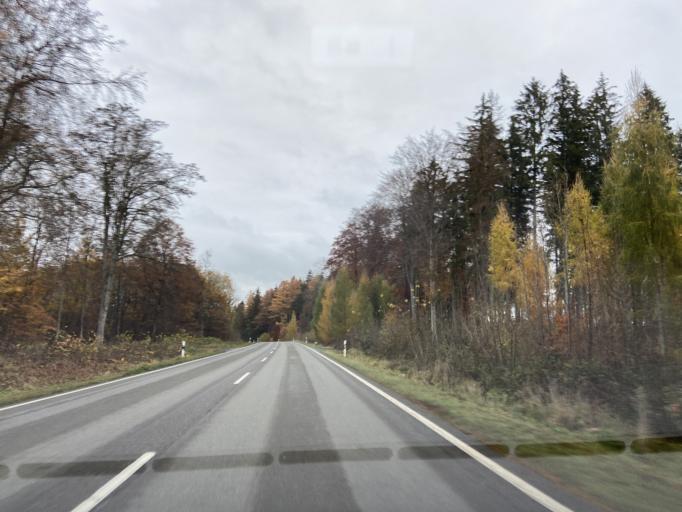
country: DE
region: Baden-Wuerttemberg
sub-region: Tuebingen Region
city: Messkirch
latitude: 47.9757
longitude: 9.1447
